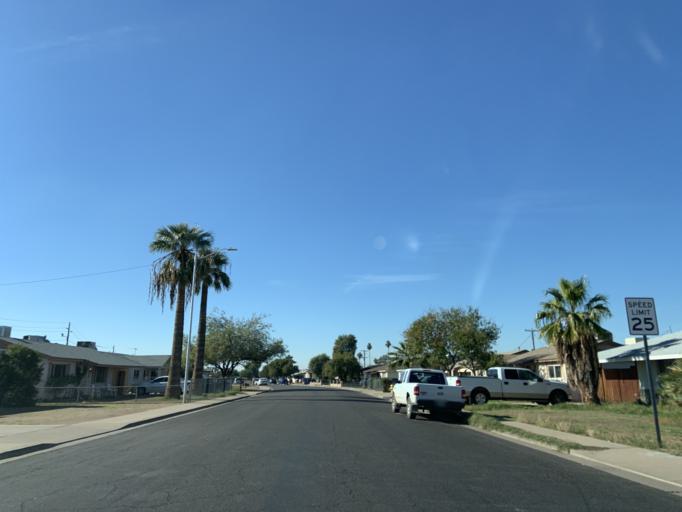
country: US
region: Arizona
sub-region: Maricopa County
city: Mesa
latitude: 33.4162
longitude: -111.8657
